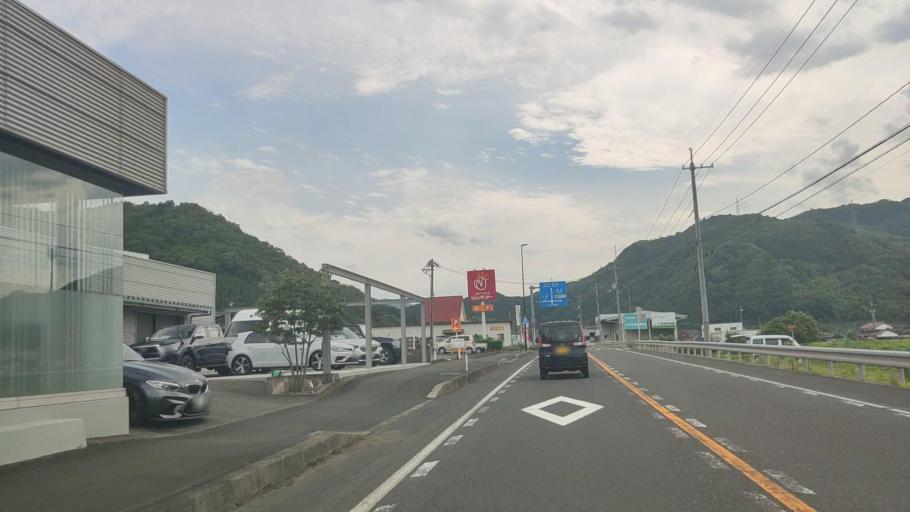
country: JP
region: Tottori
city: Tottori
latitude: 35.3566
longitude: 134.2078
